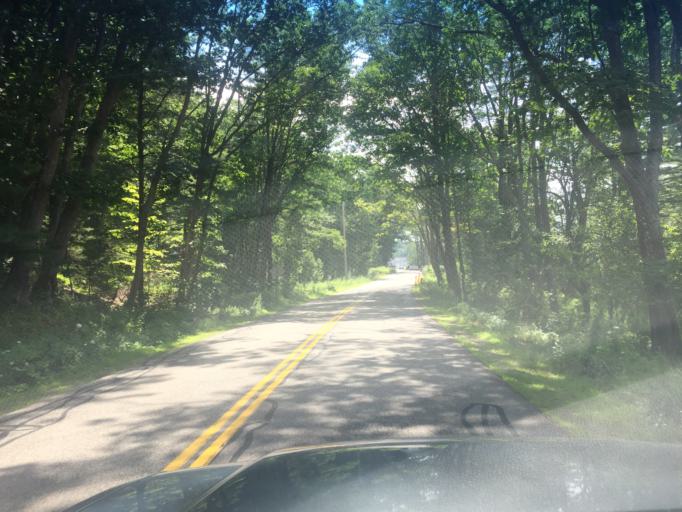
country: US
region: Maine
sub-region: York County
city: Cape Neddick
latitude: 43.1926
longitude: -70.6063
